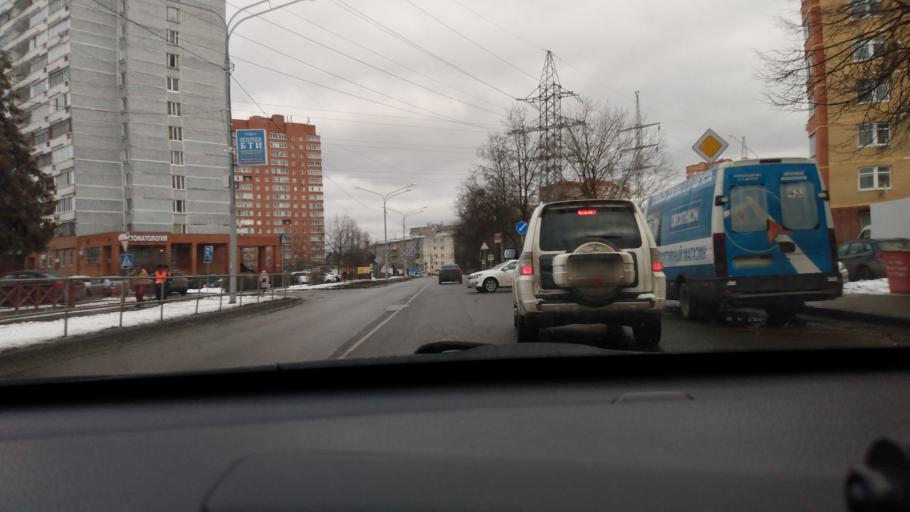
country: RU
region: Moskovskaya
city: Troitsk
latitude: 55.4893
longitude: 37.3011
